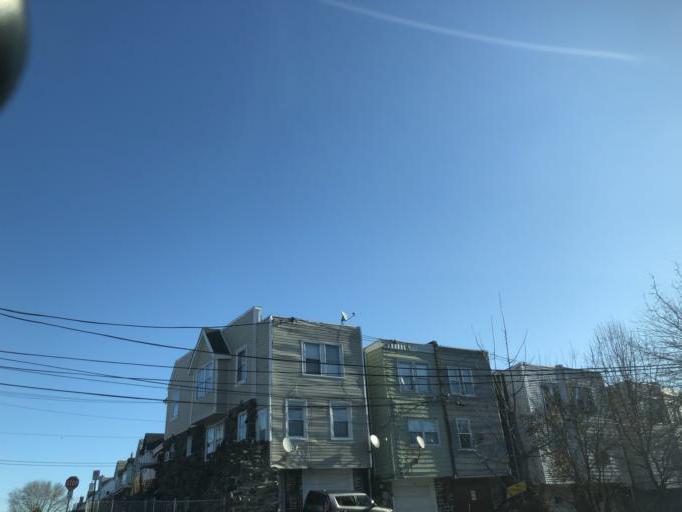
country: US
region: Pennsylvania
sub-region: Delaware County
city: East Lansdowne
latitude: 39.9534
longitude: -75.2686
